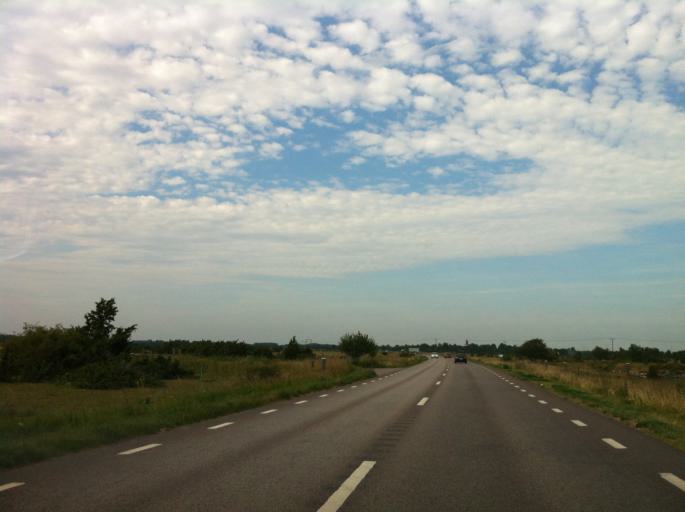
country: SE
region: Kalmar
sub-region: Borgholms Kommun
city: Borgholm
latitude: 56.9355
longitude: 16.7724
